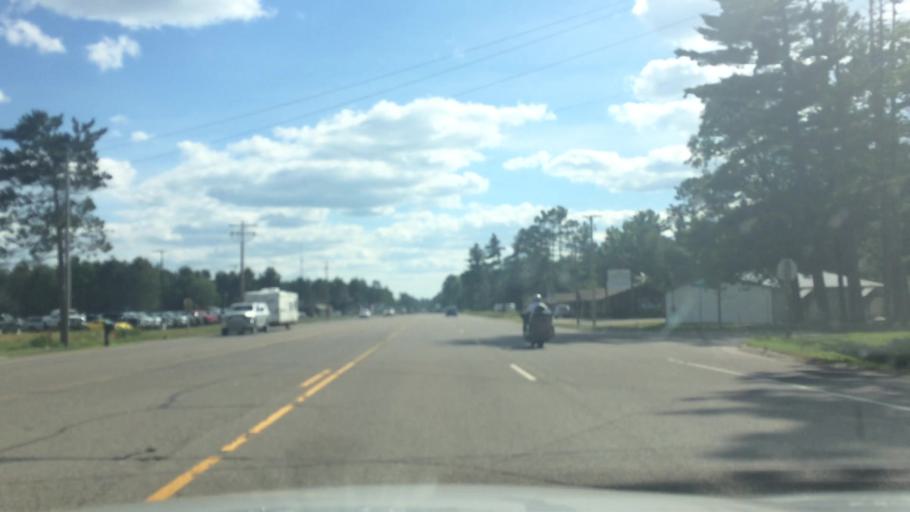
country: US
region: Wisconsin
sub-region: Vilas County
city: Lac du Flambeau
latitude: 45.8324
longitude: -89.7147
